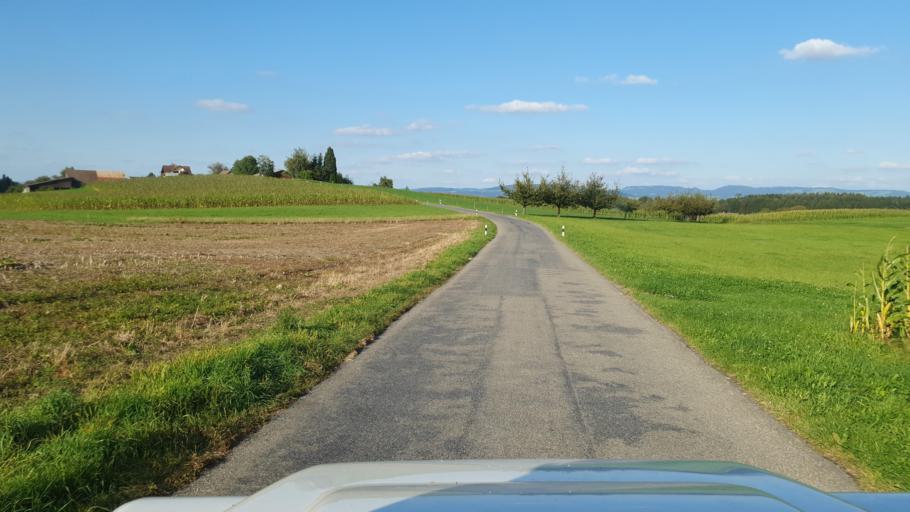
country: CH
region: Aargau
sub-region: Bezirk Muri
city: Oberruti
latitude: 47.1779
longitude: 8.3698
